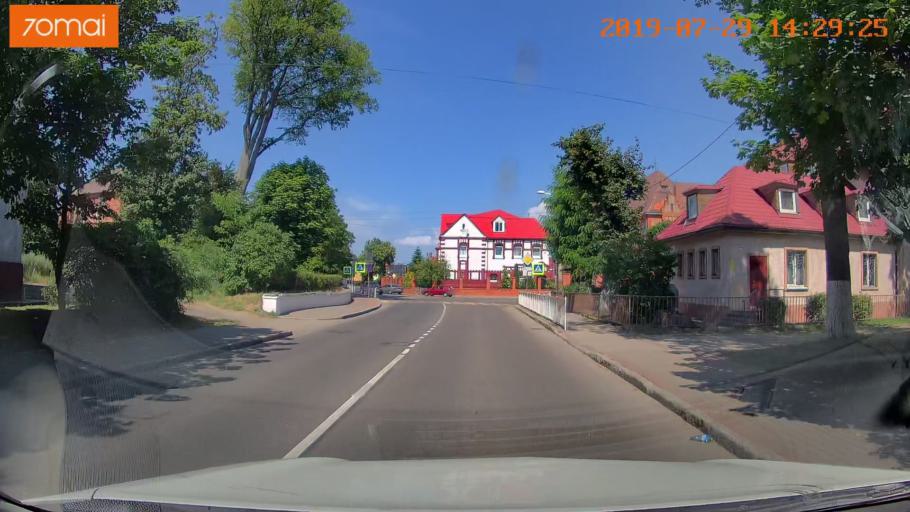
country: RU
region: Kaliningrad
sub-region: Gorod Kaliningrad
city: Baltiysk
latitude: 54.6434
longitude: 19.8920
